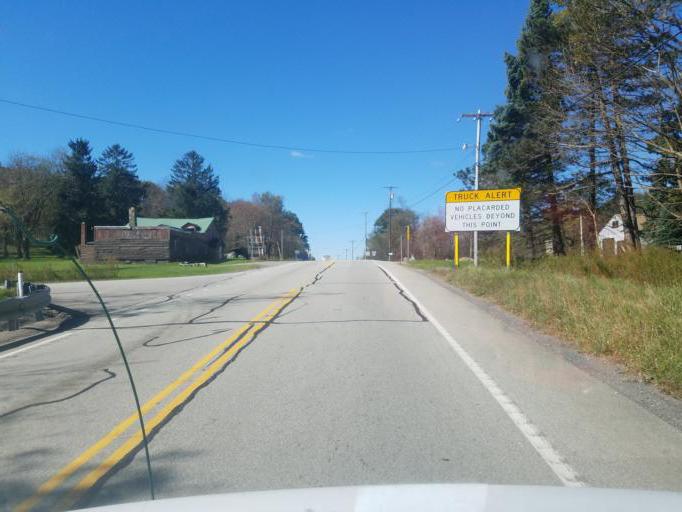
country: US
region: Pennsylvania
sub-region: Westmoreland County
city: Waterford
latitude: 40.1794
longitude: -79.1307
